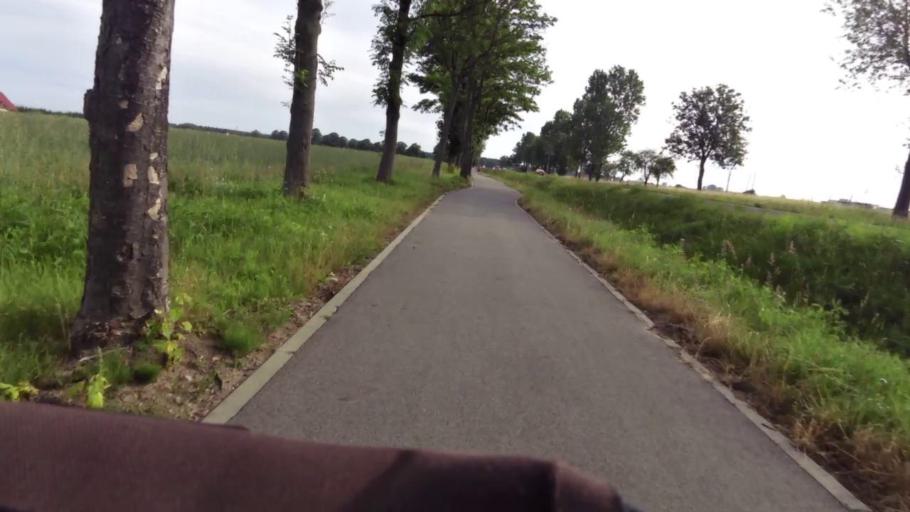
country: PL
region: West Pomeranian Voivodeship
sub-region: Powiat kamienski
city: Kamien Pomorski
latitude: 53.9828
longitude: 14.7971
